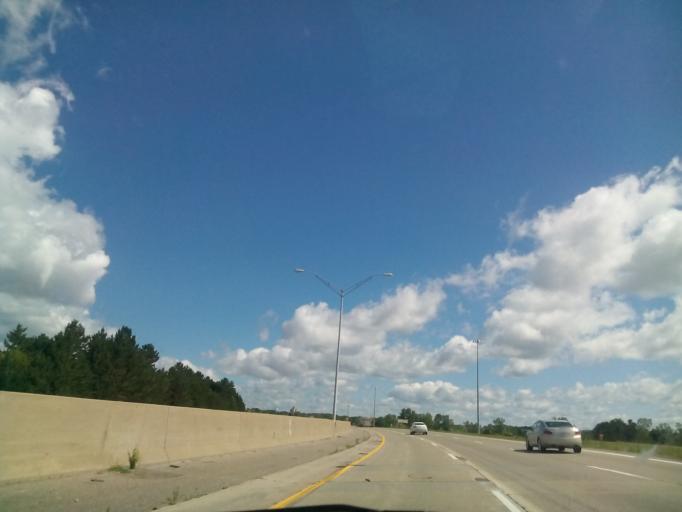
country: US
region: Michigan
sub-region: Genesee County
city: Flint
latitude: 42.9927
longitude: -83.7097
